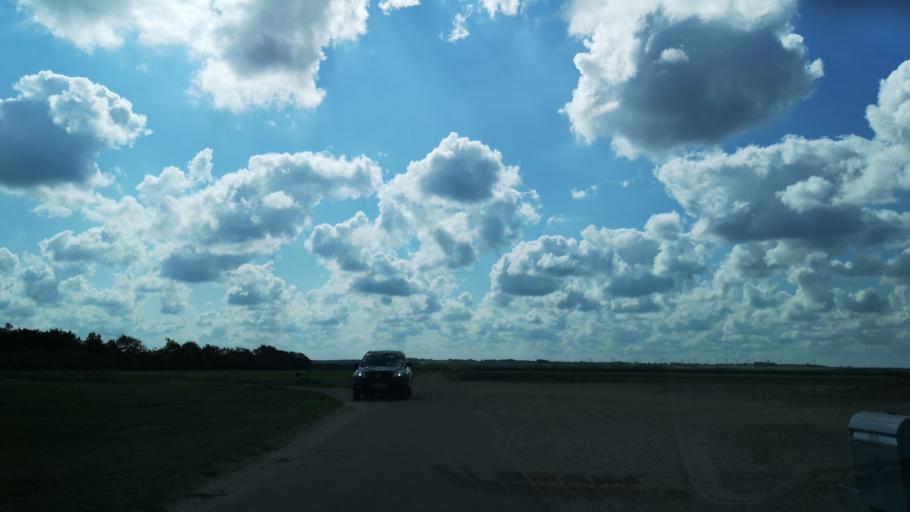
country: DK
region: Central Jutland
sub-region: Ringkobing-Skjern Kommune
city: Skjern
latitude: 55.9327
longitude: 8.4608
